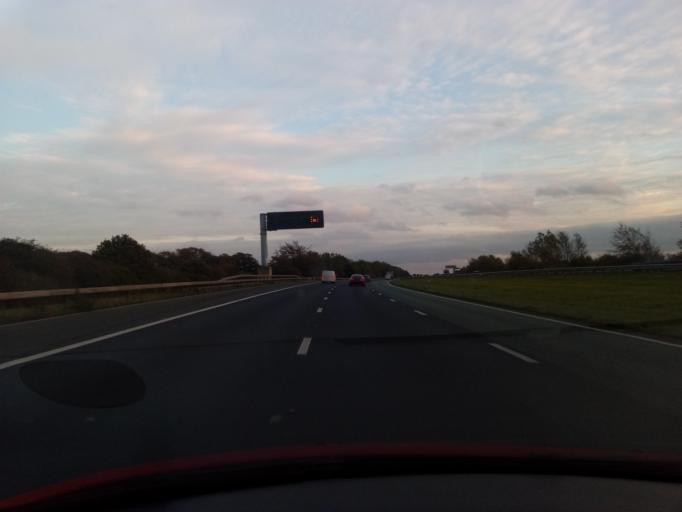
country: GB
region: England
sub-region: City and Borough of Leeds
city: Wetherby
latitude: 53.9082
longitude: -1.3805
